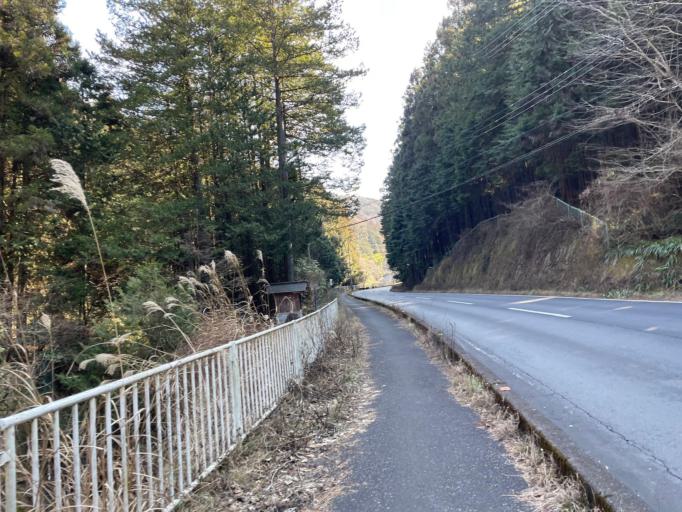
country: JP
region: Saitama
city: Hanno
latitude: 35.8527
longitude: 139.2499
